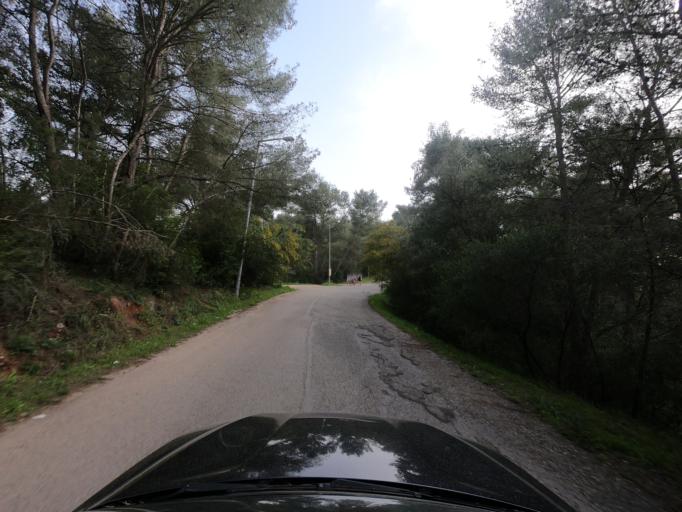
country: PT
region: Setubal
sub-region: Setubal
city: Setubal
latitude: 38.5196
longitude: -8.9085
